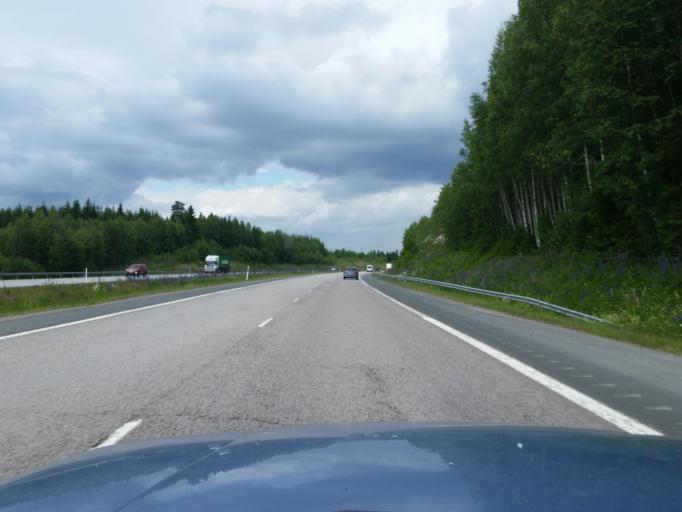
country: FI
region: Paijanne Tavastia
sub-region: Lahti
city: Nastola
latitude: 61.0223
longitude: 25.8302
